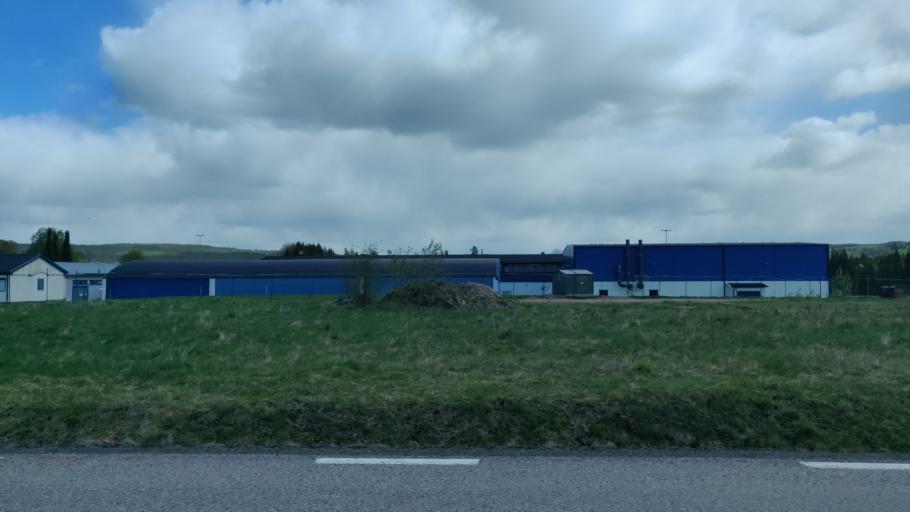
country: SE
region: Vaermland
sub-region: Karlstads Kommun
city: Molkom
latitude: 59.6051
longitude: 13.7387
